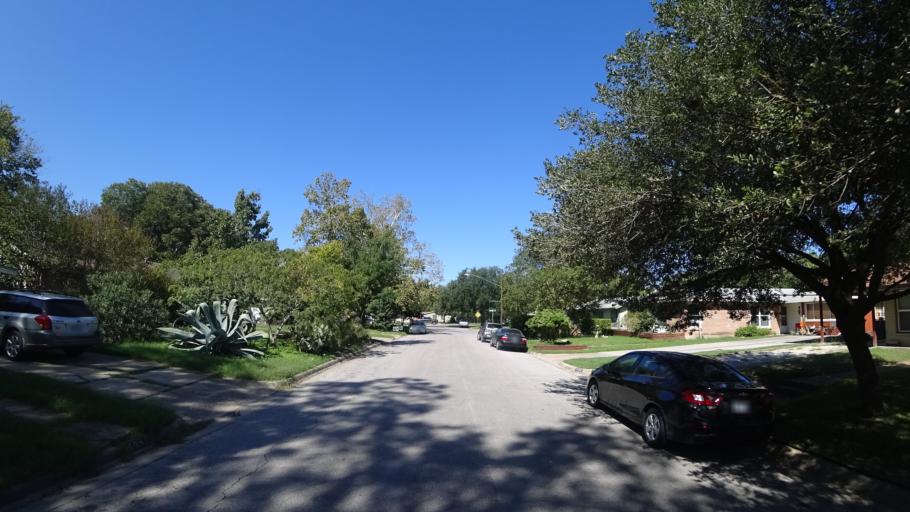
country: US
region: Texas
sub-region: Travis County
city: Austin
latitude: 30.3101
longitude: -97.7015
